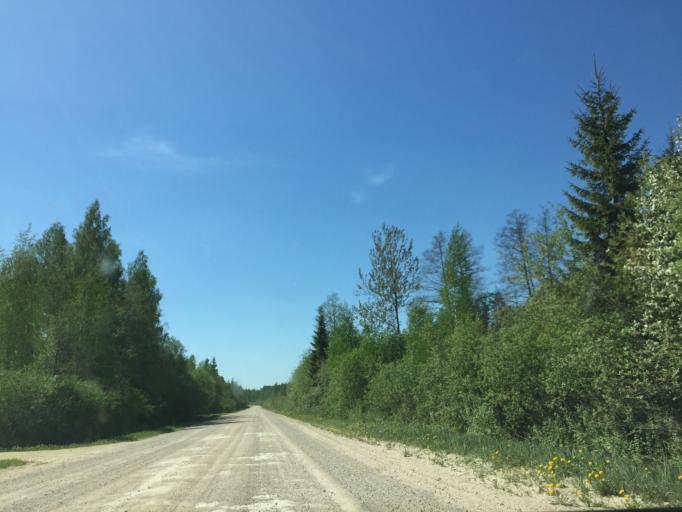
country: LV
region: Kegums
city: Kegums
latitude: 56.8827
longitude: 24.7858
